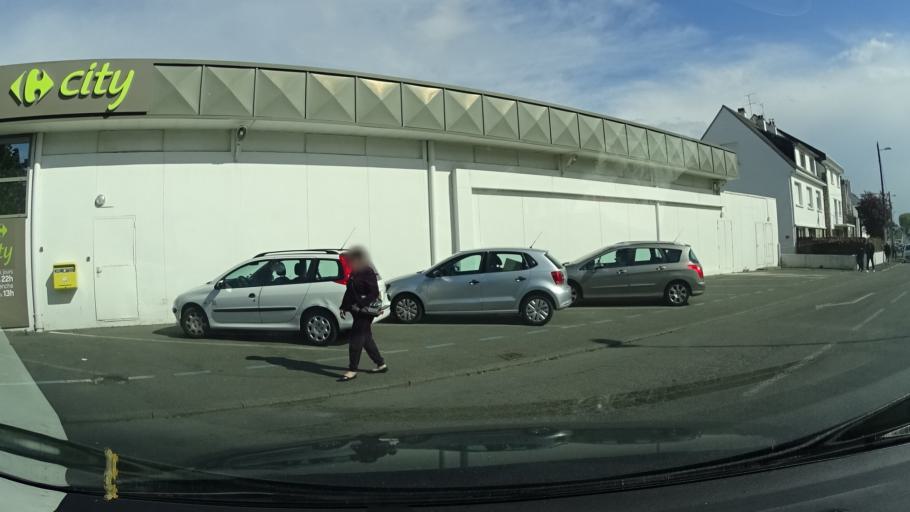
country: FR
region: Brittany
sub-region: Departement du Morbihan
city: Vannes
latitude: 47.6501
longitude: -2.7702
